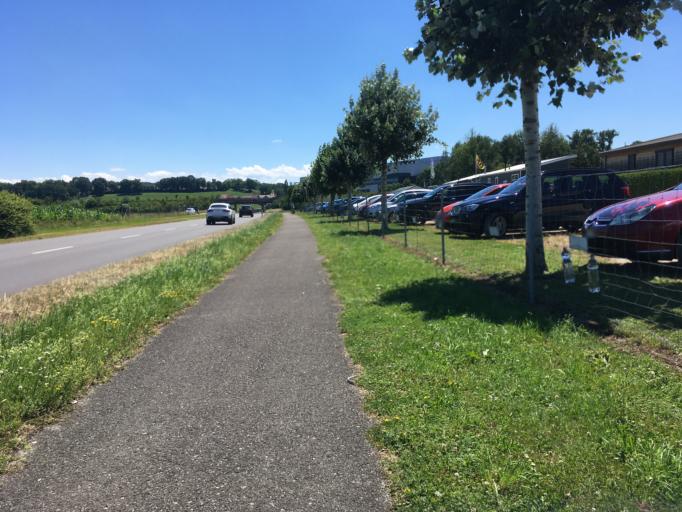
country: CH
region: Vaud
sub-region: Broye-Vully District
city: Avenches
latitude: 46.8979
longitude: 7.0508
